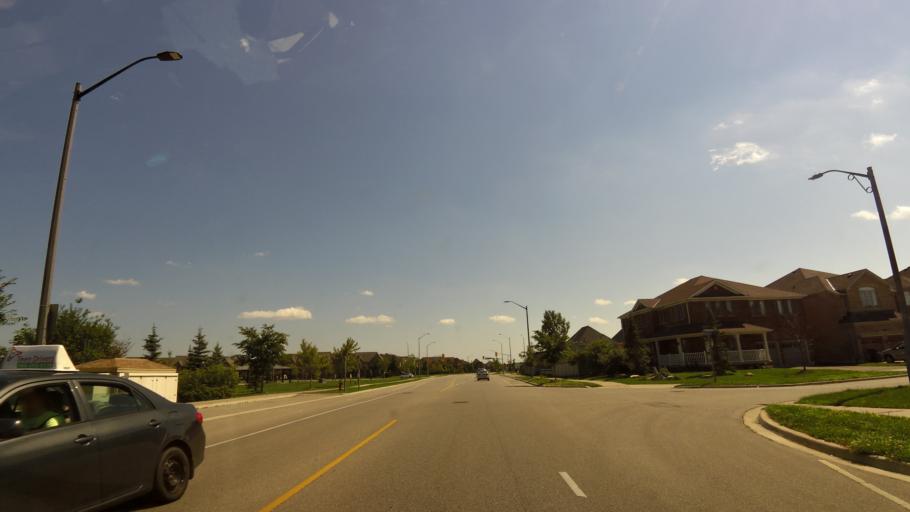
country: CA
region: Ontario
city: Mississauga
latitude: 43.5490
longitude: -79.7286
